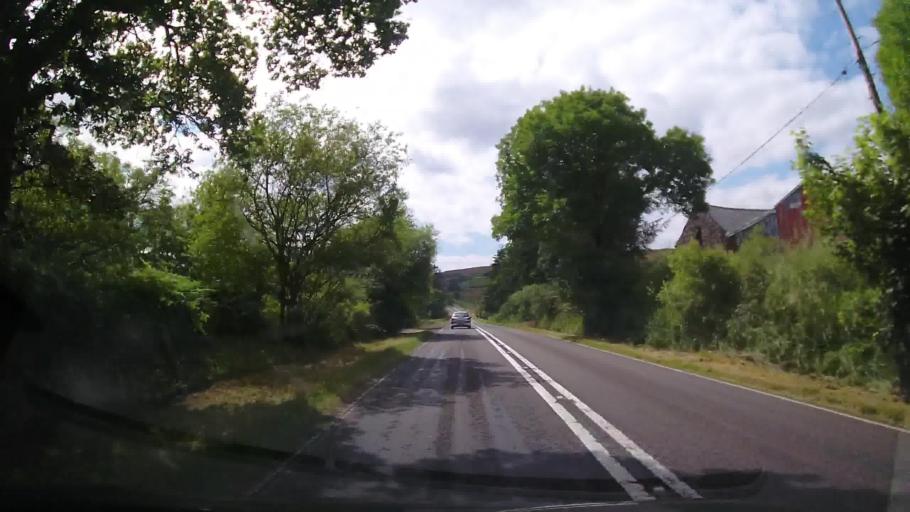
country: GB
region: Wales
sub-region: Gwynedd
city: Trawsfynydd
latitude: 52.9083
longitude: -3.8764
